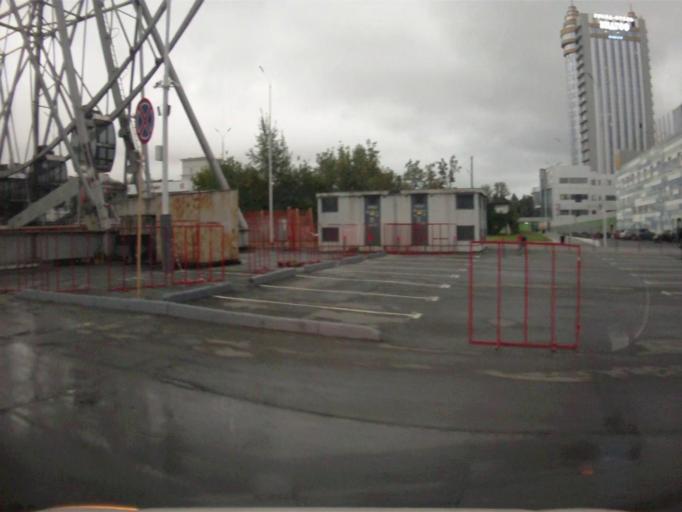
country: RU
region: Chelyabinsk
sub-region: Gorod Chelyabinsk
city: Chelyabinsk
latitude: 55.1642
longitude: 61.4326
